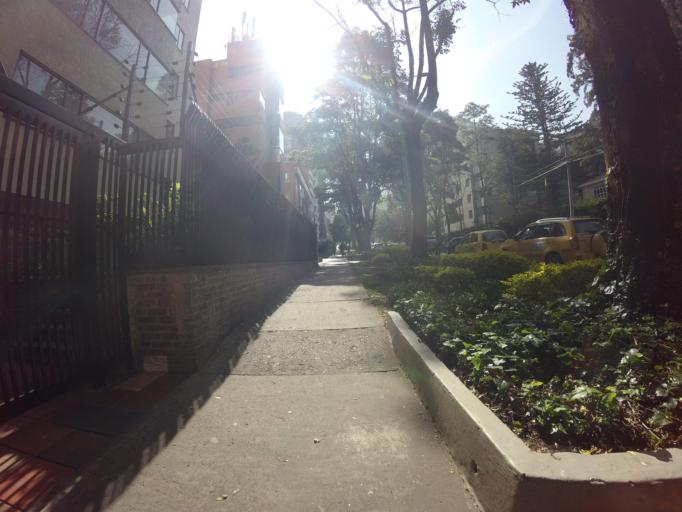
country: CO
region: Bogota D.C.
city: Barrio San Luis
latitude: 4.6604
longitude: -74.0535
